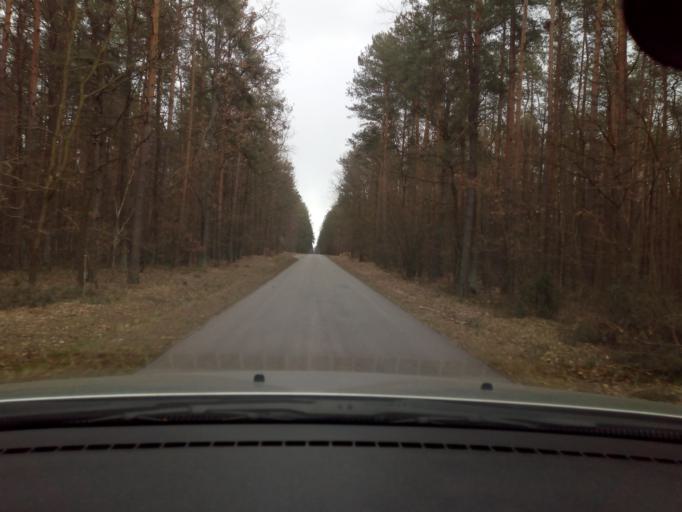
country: PL
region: Swietokrzyskie
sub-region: Powiat starachowicki
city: Brody
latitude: 51.0709
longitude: 21.3129
